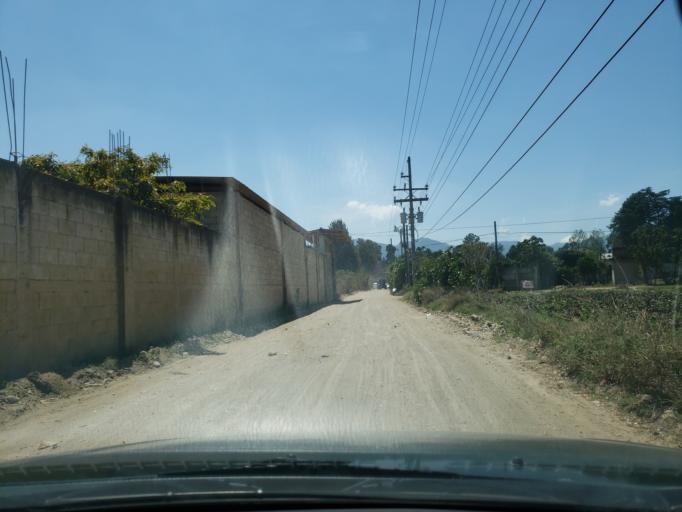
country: GT
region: Chimaltenango
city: El Tejar
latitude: 14.6441
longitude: -90.8071
